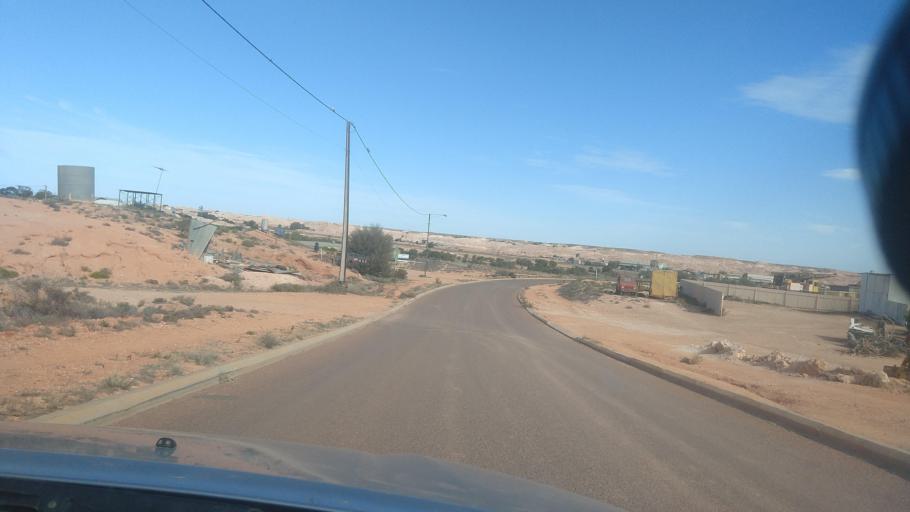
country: AU
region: South Australia
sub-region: Coober Pedy
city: Coober Pedy
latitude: -29.0138
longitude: 134.7491
